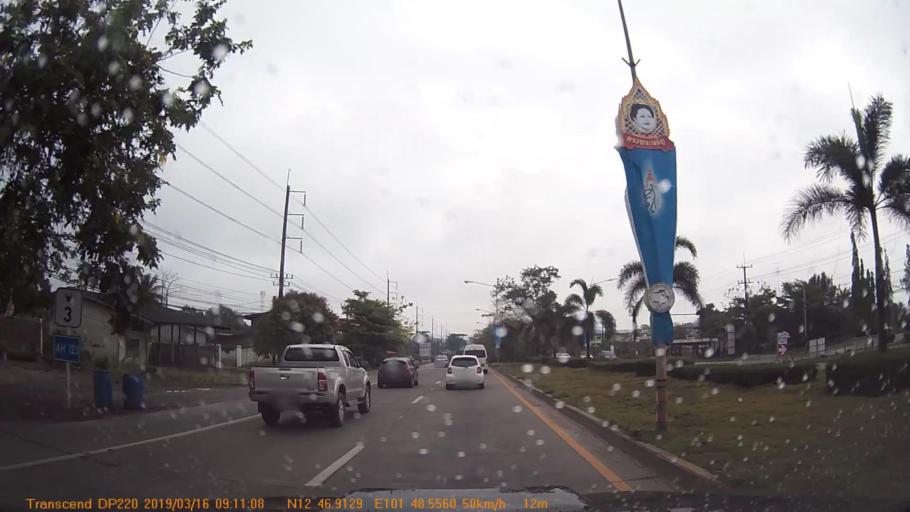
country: TH
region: Chanthaburi
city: Na Yai Am
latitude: 12.7819
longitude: 101.8094
